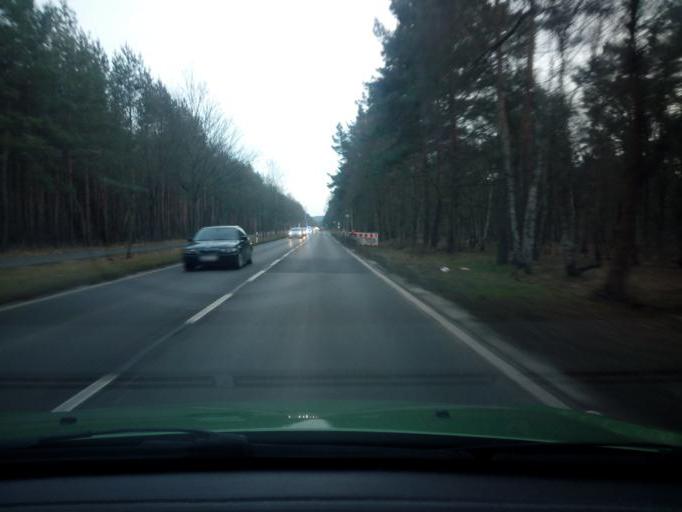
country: DE
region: Berlin
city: Berlin Koepenick
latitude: 52.4358
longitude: 13.5998
